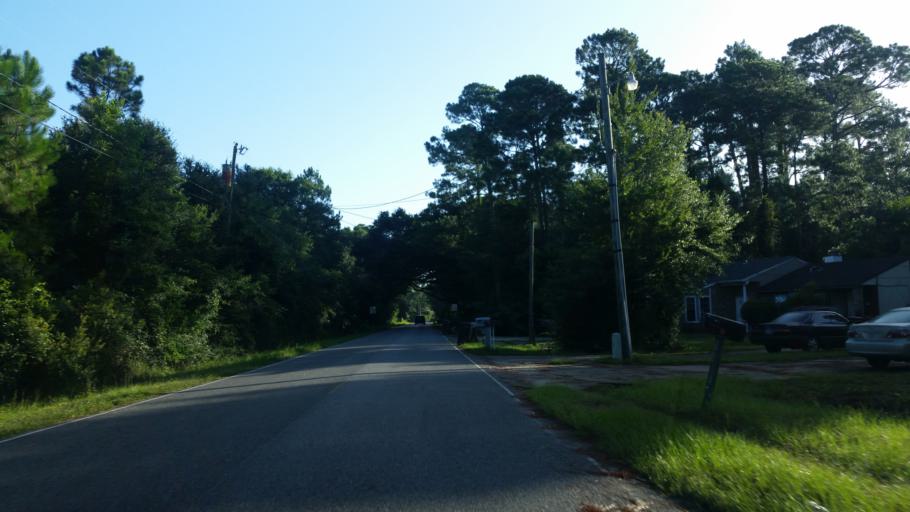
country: US
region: Florida
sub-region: Escambia County
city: Myrtle Grove
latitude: 30.4116
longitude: -87.3222
